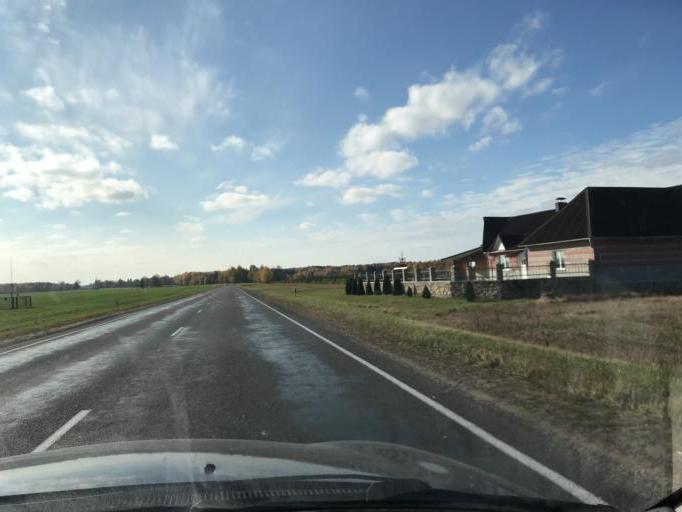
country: BY
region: Grodnenskaya
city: Voranava
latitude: 54.1881
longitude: 25.3410
